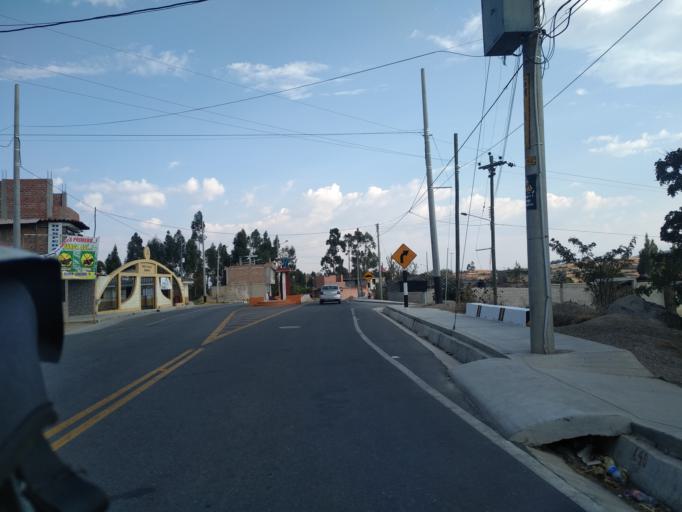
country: PE
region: Cajamarca
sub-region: San Marcos
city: La Grama
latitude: -7.3914
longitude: -78.1238
